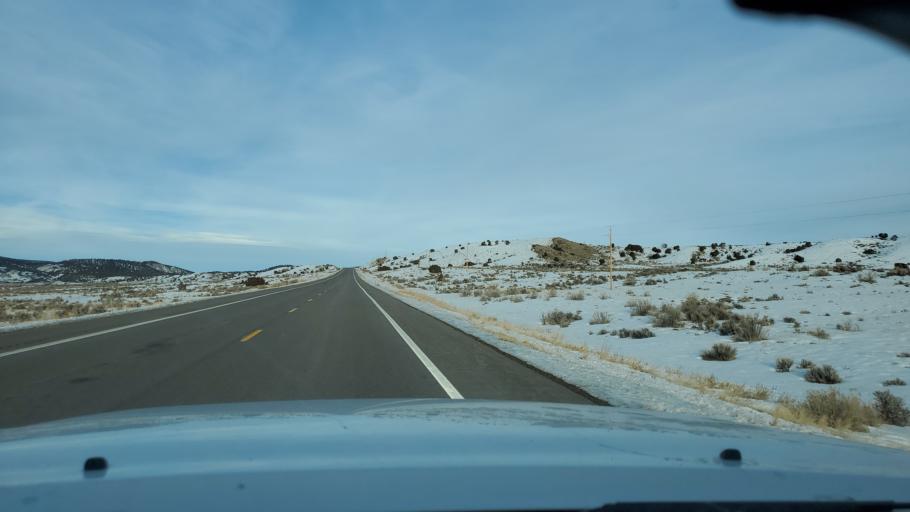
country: US
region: Colorado
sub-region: Rio Blanco County
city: Rangely
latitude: 40.3225
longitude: -108.5047
